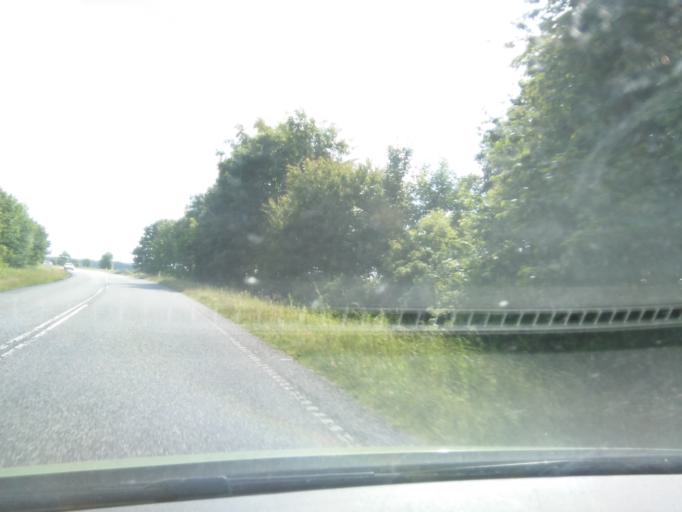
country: DK
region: Central Jutland
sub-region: Odder Kommune
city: Odder
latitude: 55.9669
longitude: 10.0823
